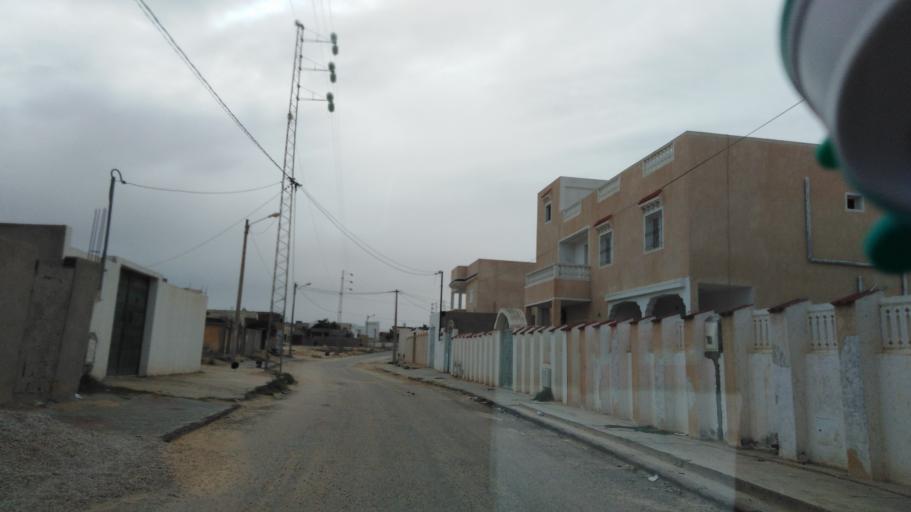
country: TN
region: Qabis
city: Gabes
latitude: 33.9547
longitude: 10.0042
